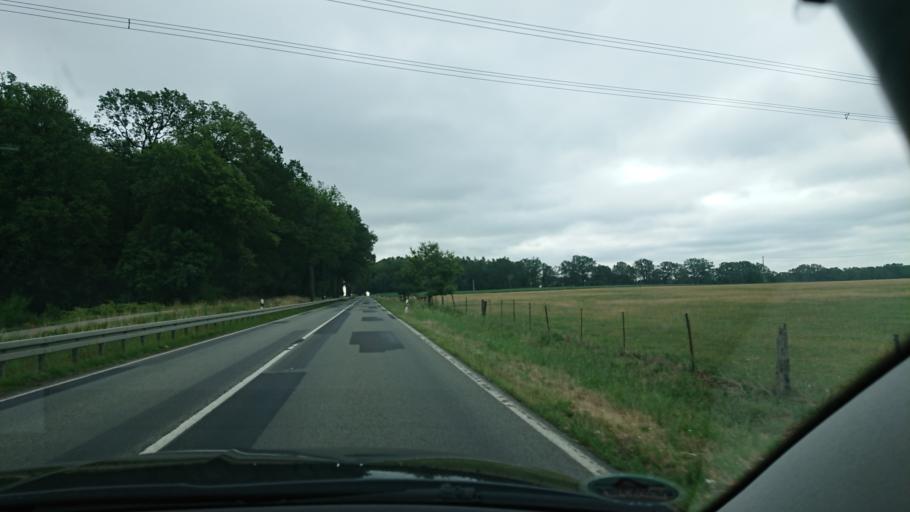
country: DE
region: Brandenburg
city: Bad Wilsnack
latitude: 53.0296
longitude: 11.9753
